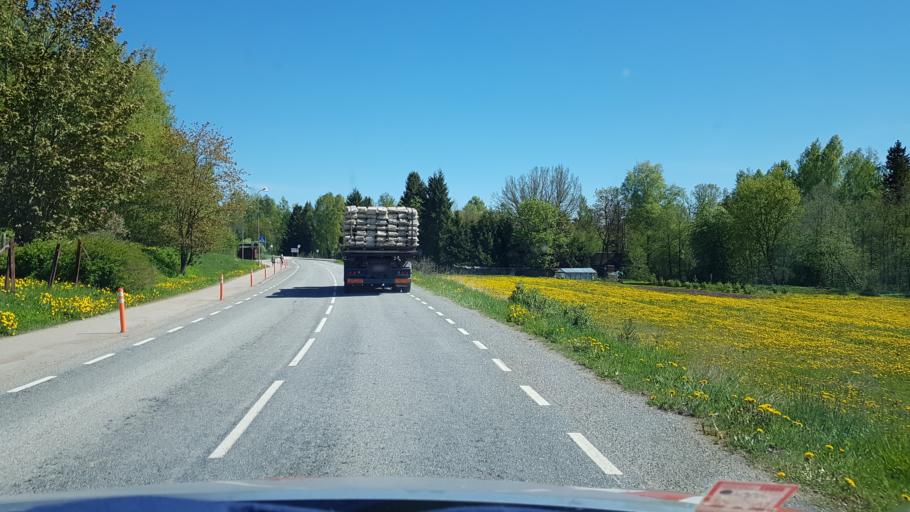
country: EE
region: Tartu
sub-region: UElenurme vald
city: Ulenurme
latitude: 58.2942
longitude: 26.8897
